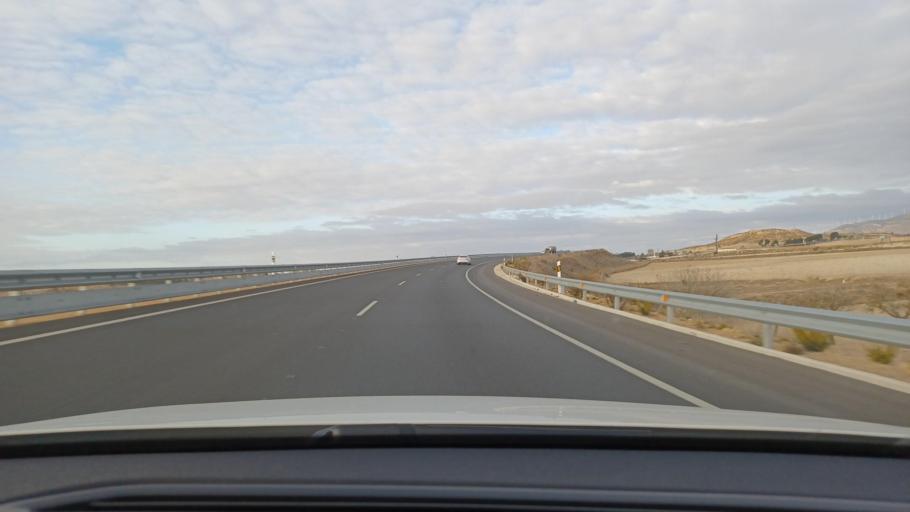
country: ES
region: Castille-La Mancha
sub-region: Provincia de Albacete
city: Caudete
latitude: 38.7316
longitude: -0.9295
